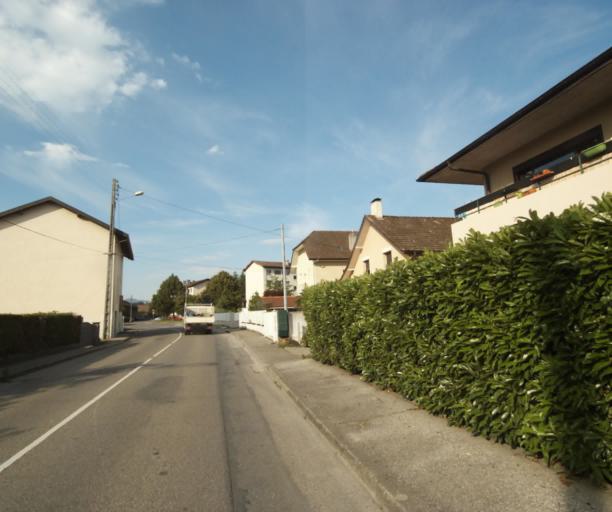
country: FR
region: Rhone-Alpes
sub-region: Departement de la Haute-Savoie
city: Thonon-les-Bains
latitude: 46.3817
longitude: 6.5038
